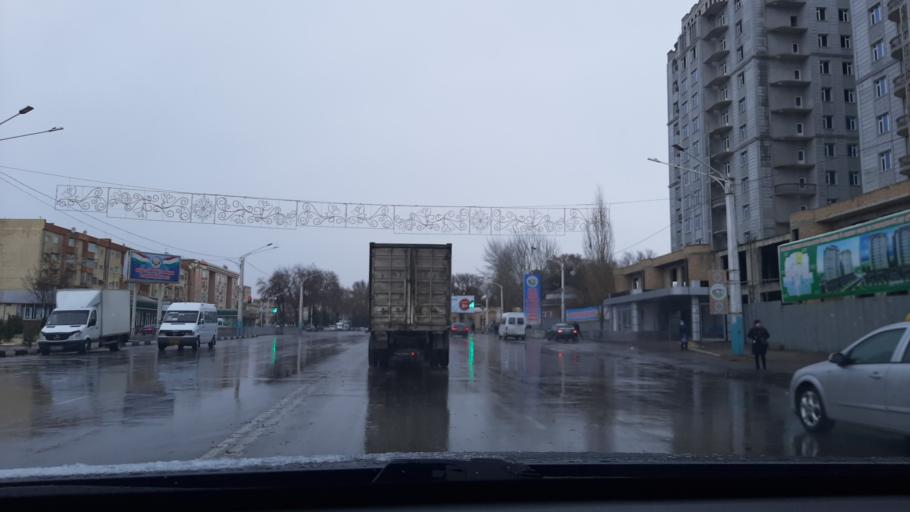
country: TJ
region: Viloyati Sughd
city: Khujand
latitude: 40.2720
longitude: 69.6426
